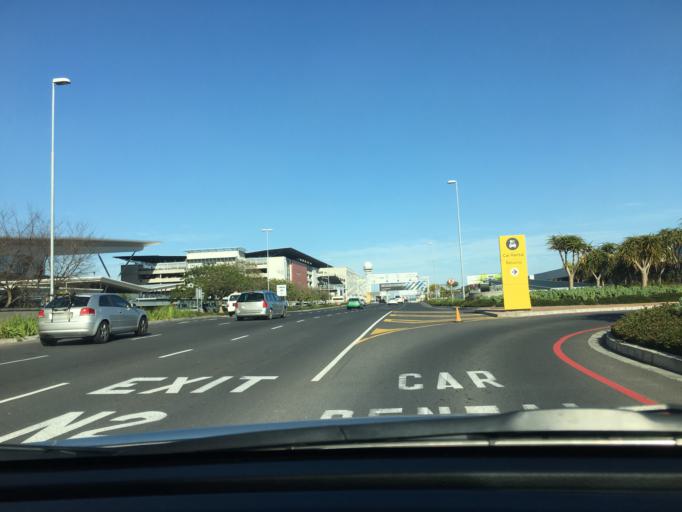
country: ZA
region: Western Cape
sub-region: City of Cape Town
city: Lansdowne
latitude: -33.9687
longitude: 18.5951
